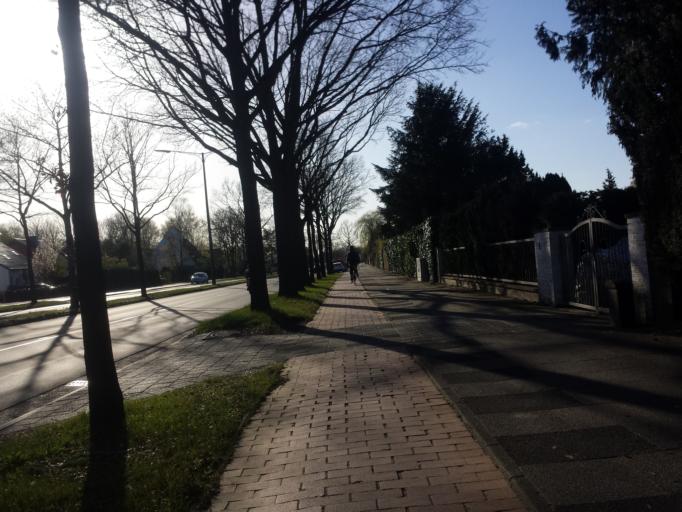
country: DE
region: Lower Saxony
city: Lilienthal
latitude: 53.0714
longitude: 8.9094
